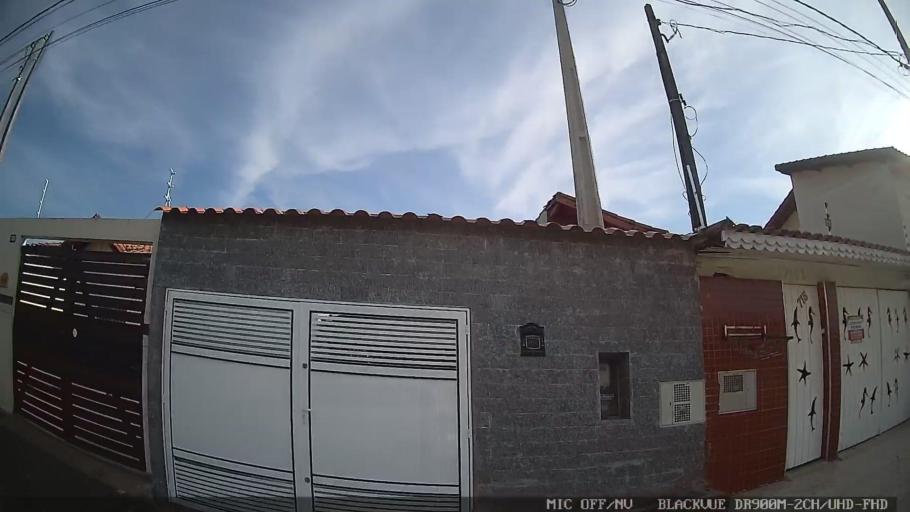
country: BR
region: Sao Paulo
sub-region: Itanhaem
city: Itanhaem
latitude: -24.1619
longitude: -46.7696
